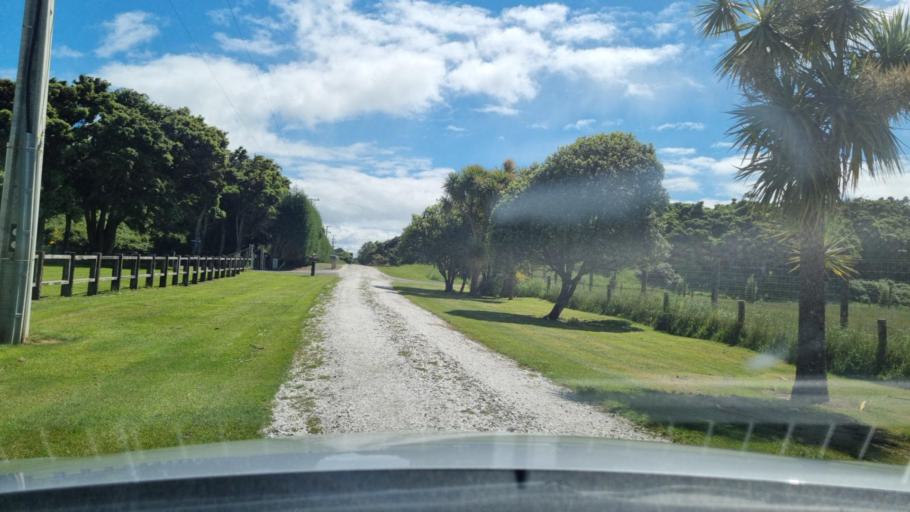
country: NZ
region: Southland
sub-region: Invercargill City
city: Invercargill
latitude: -46.4573
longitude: 168.2813
